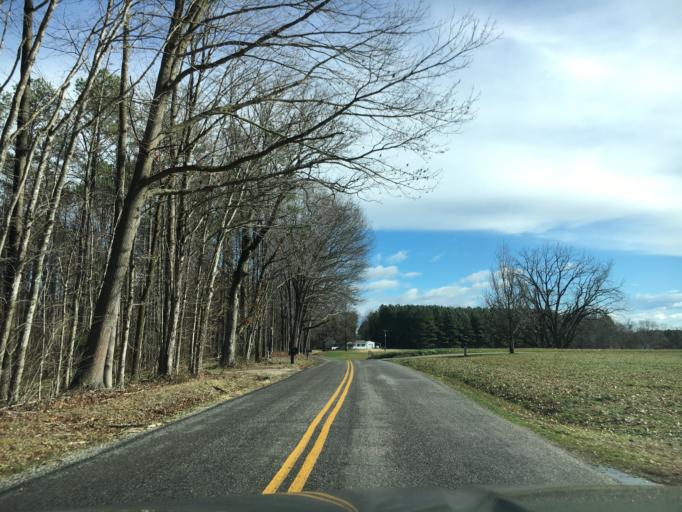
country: US
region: Virginia
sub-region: Amelia County
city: Amelia Court House
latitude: 37.4444
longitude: -78.0083
